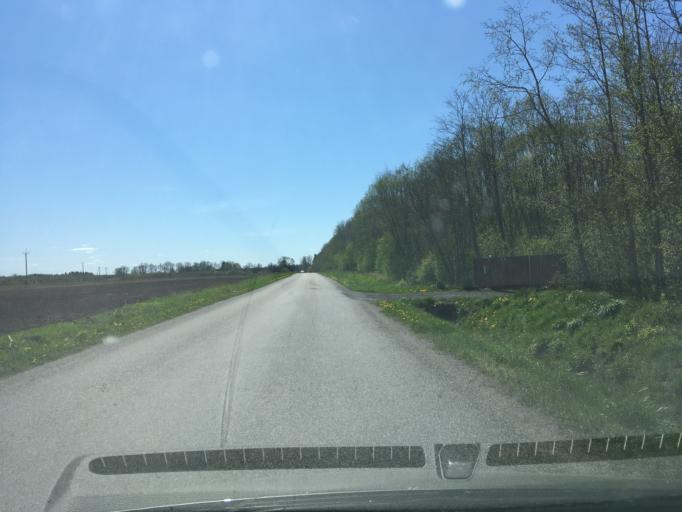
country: EE
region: Harju
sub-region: Raasiku vald
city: Arukula
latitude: 59.3984
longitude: 25.0800
